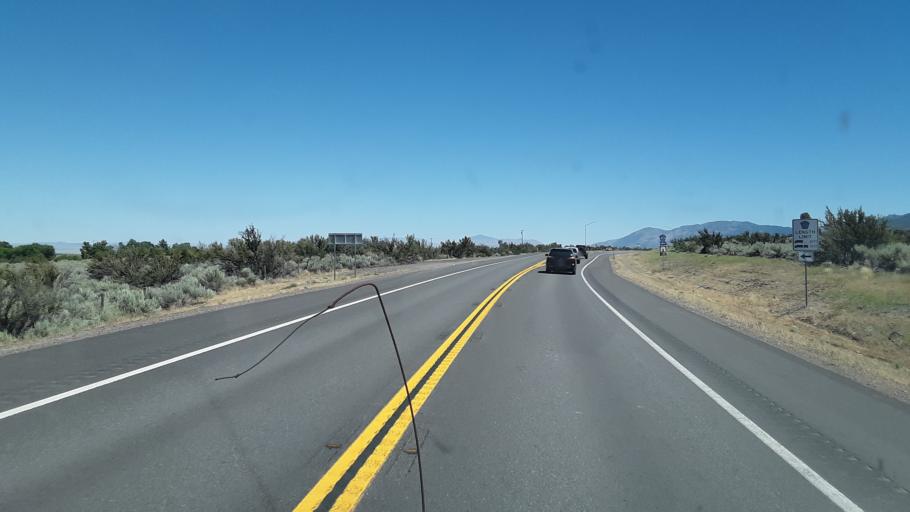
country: US
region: California
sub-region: Lassen County
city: Janesville
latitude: 40.2862
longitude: -120.4935
